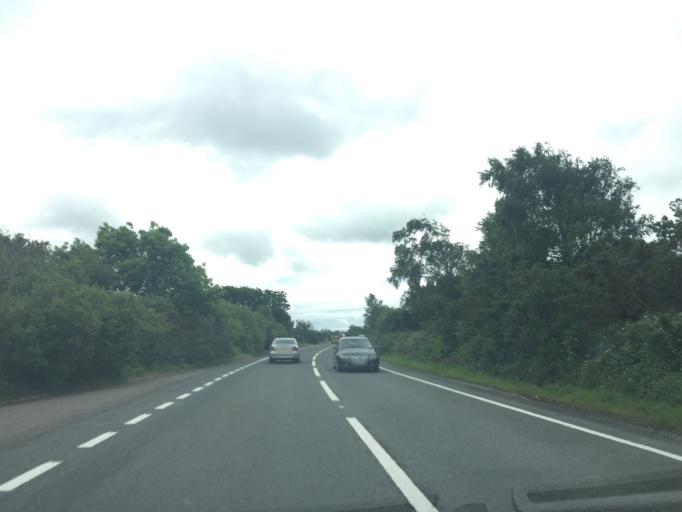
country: GB
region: England
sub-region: Dorset
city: Wareham
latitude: 50.6668
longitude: -2.0987
